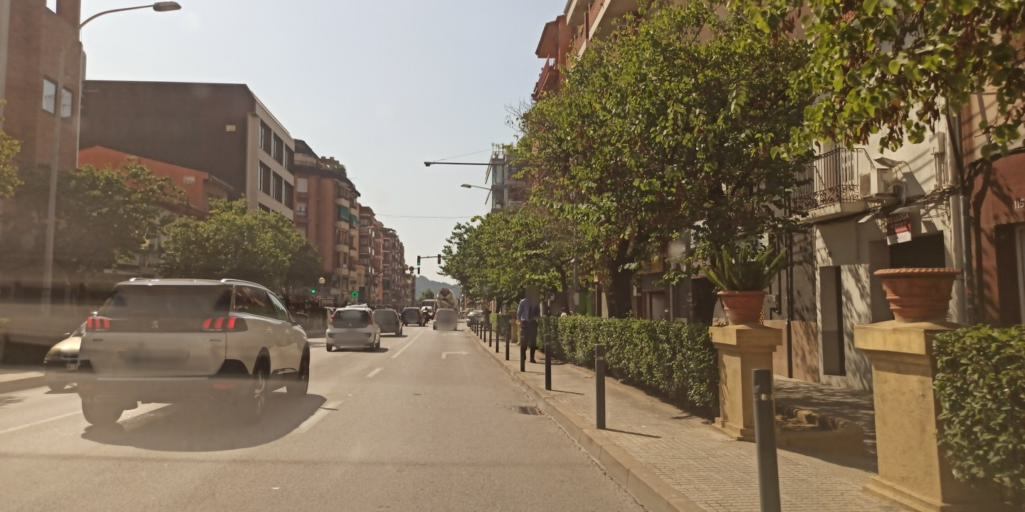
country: ES
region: Catalonia
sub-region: Provincia de Barcelona
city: Cerdanyola del Valles
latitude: 41.4938
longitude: 2.1474
